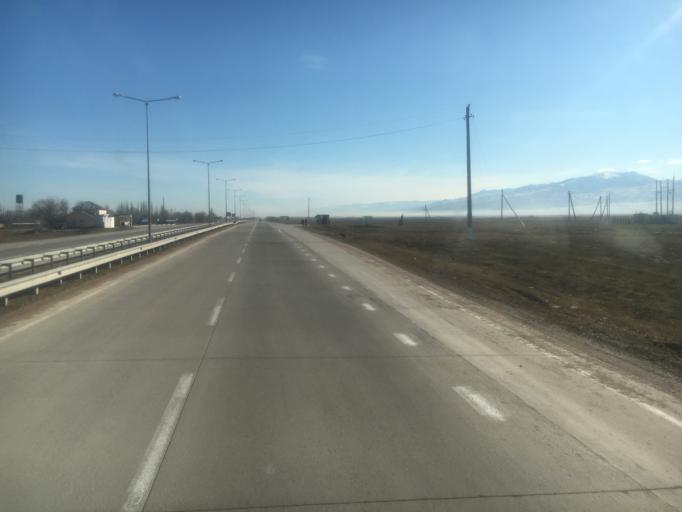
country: KZ
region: Zhambyl
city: Merke
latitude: 42.8894
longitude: 72.9830
